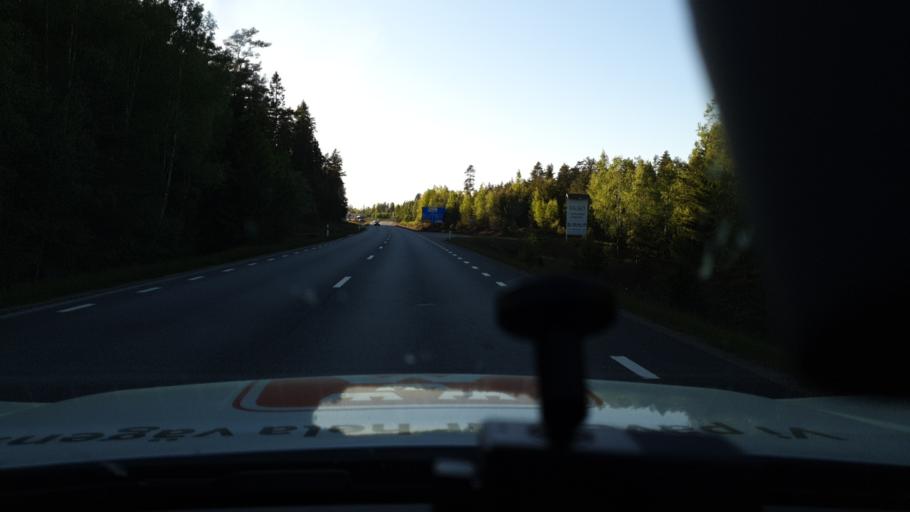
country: SE
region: Joenkoeping
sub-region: Eksjo Kommun
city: Eksjoe
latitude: 57.6447
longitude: 14.9591
